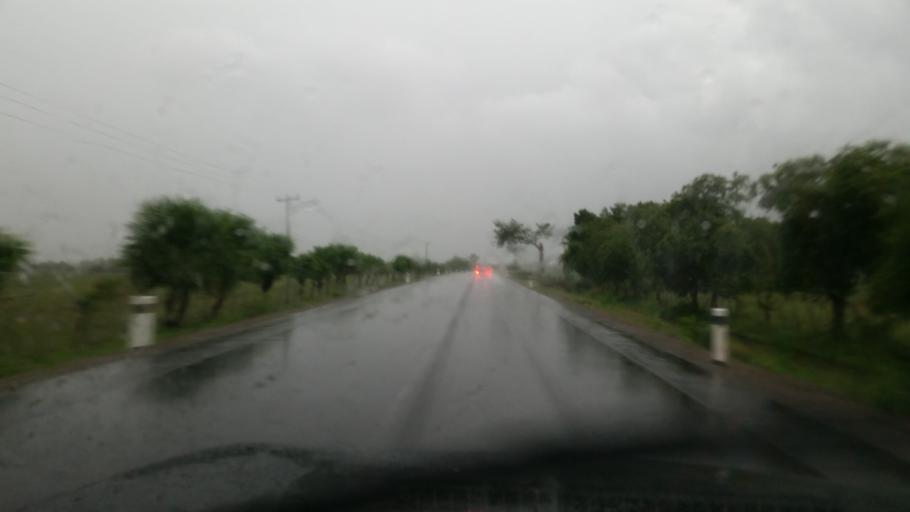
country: NI
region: Chinandega
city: Chichigalpa
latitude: 12.7750
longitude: -86.9216
